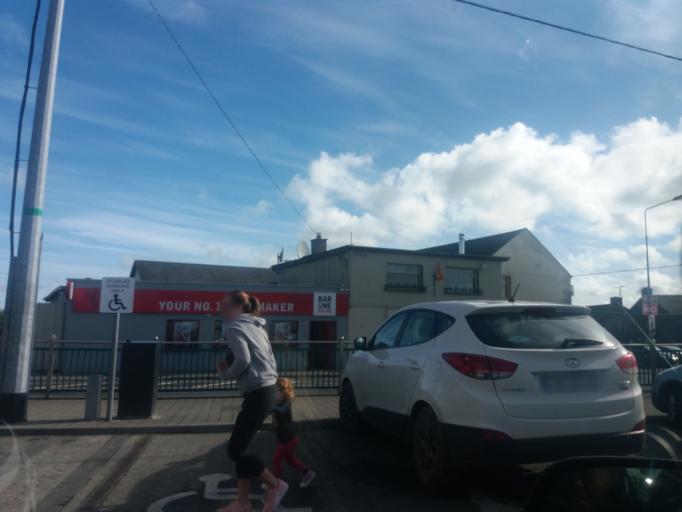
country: IE
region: Leinster
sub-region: An Mhi
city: Kells
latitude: 53.7295
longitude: -6.8822
